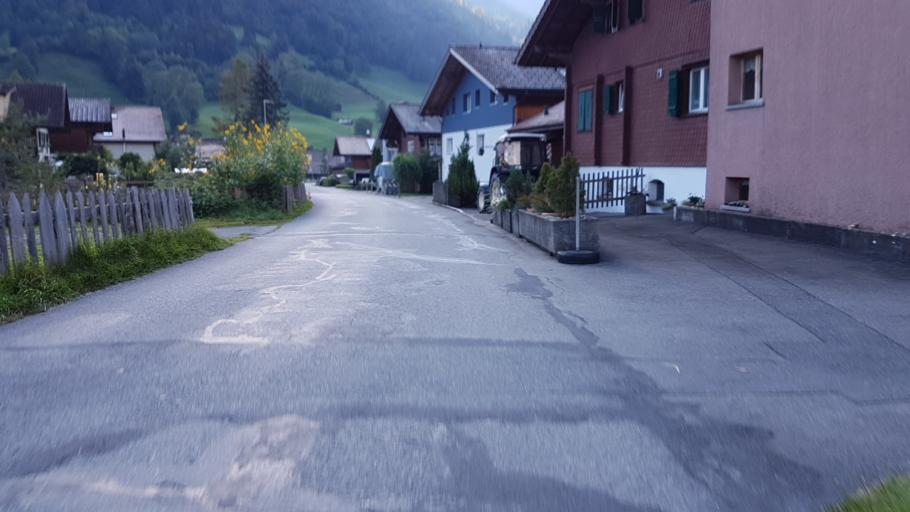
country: CH
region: Bern
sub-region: Frutigen-Niedersimmental District
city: Frutigen
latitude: 46.5840
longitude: 7.6550
